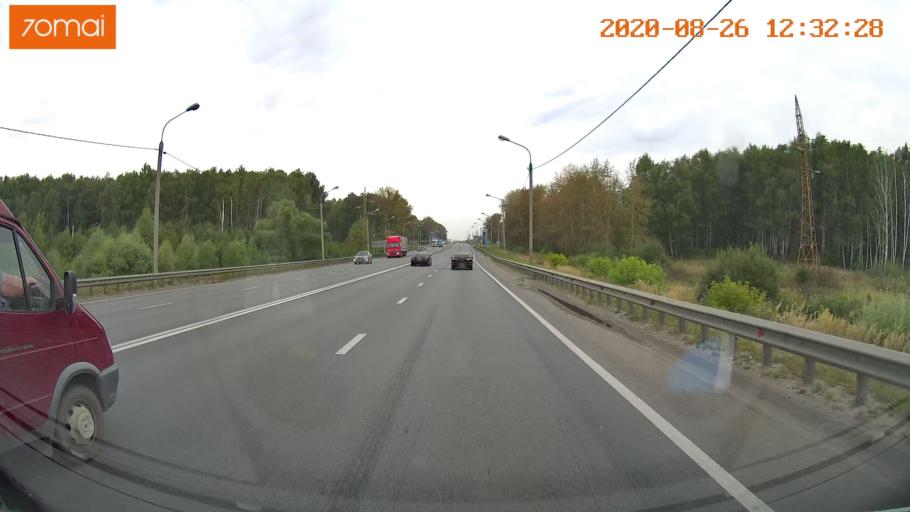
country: RU
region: Rjazan
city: Ryazan'
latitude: 54.5779
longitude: 39.7901
